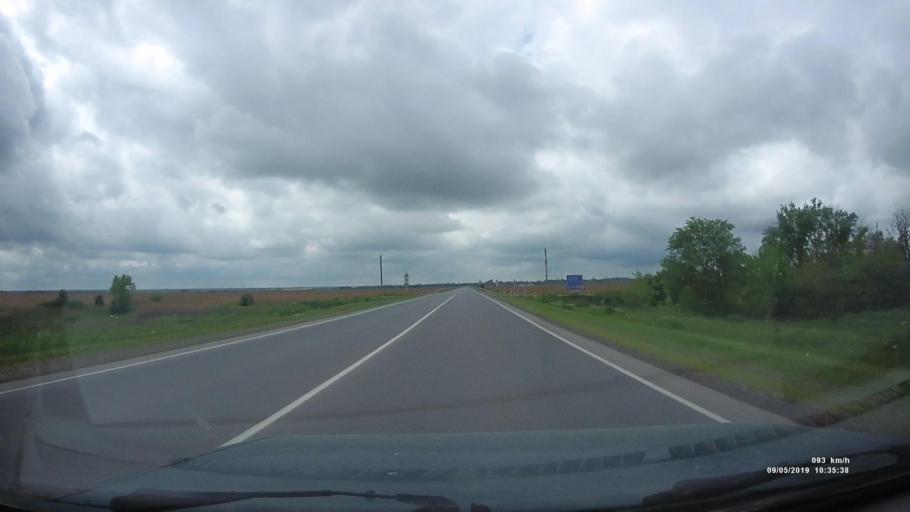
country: RU
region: Rostov
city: Peshkovo
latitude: 47.0401
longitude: 39.4126
